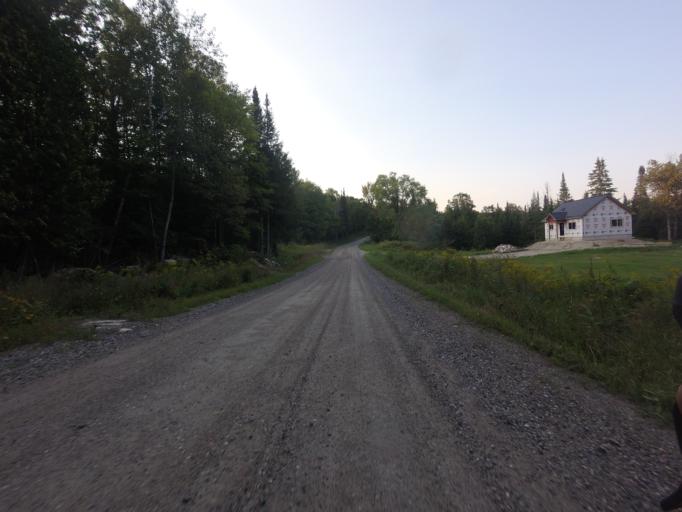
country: CA
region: Ontario
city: Renfrew
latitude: 45.0382
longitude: -76.7419
